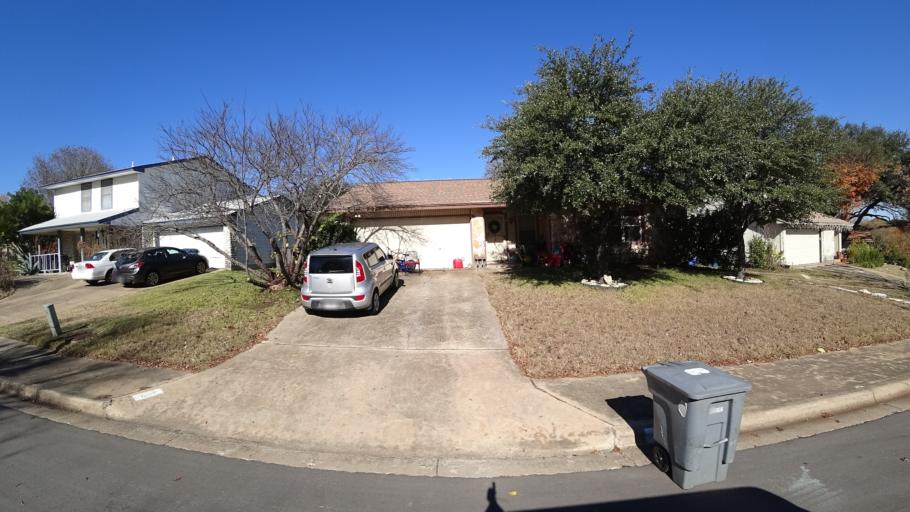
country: US
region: Texas
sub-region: Travis County
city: Wells Branch
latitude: 30.4144
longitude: -97.7140
